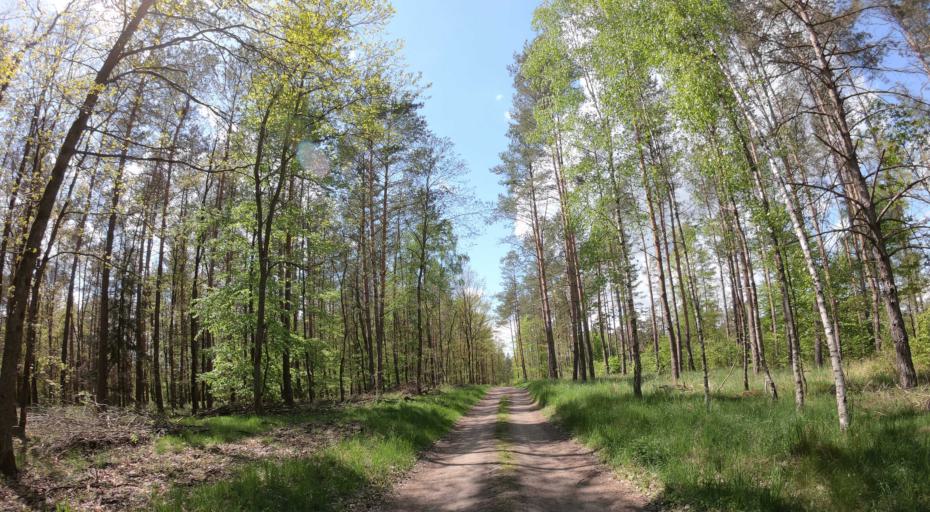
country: PL
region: West Pomeranian Voivodeship
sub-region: Powiat lobeski
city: Lobez
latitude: 53.5971
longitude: 15.6339
